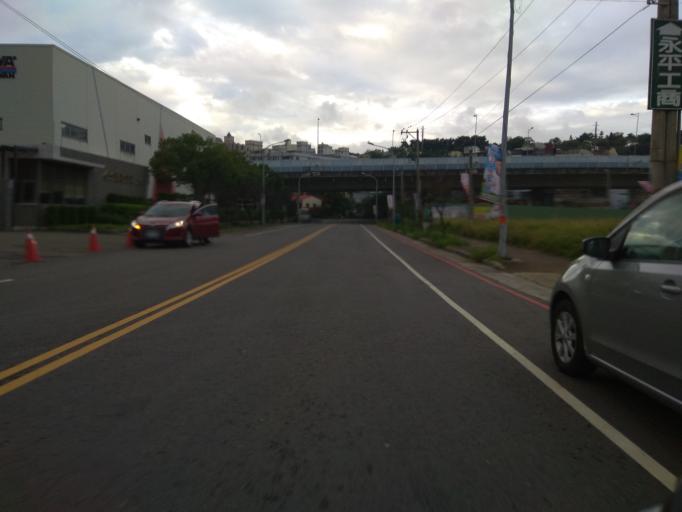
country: TW
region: Taiwan
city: Daxi
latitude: 24.9201
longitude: 121.1827
